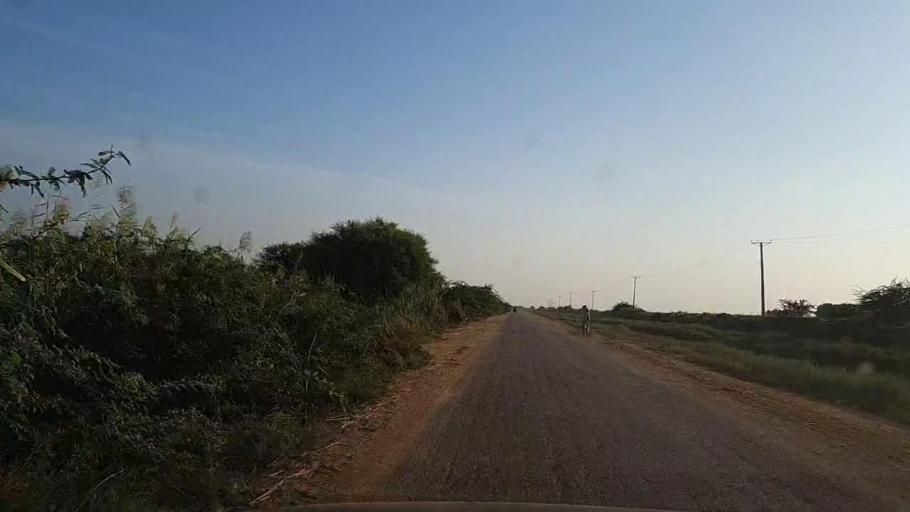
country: PK
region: Sindh
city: Thatta
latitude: 24.6440
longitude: 67.9125
